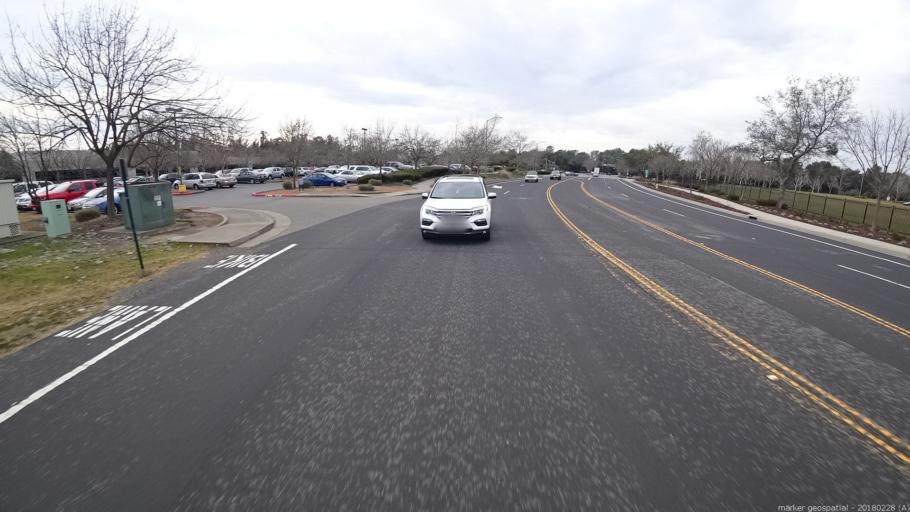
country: US
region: California
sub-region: Sacramento County
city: Folsom
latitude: 38.6637
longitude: -121.1810
